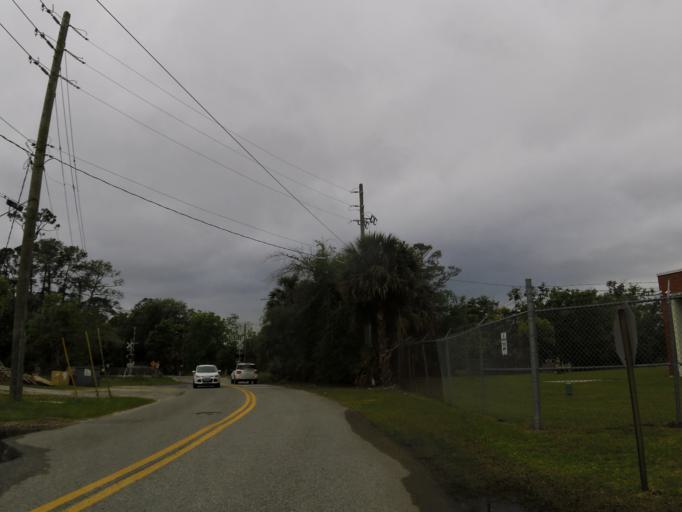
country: US
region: Florida
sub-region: Duval County
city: Jacksonville
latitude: 30.3003
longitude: -81.6444
